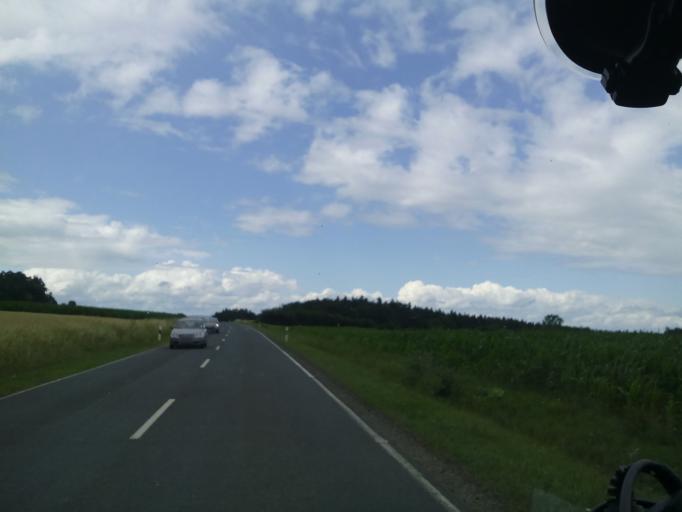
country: DE
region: Bavaria
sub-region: Upper Franconia
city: Rodental
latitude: 50.2563
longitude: 11.0853
